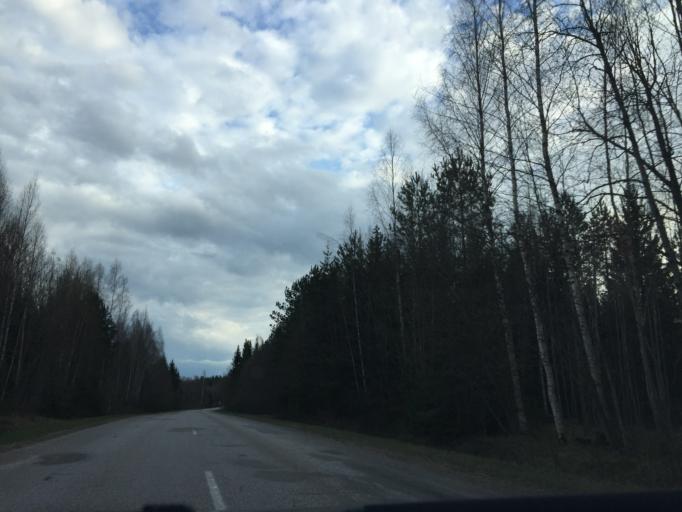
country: LV
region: Aluksnes Rajons
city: Aluksne
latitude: 57.3099
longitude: 27.0715
